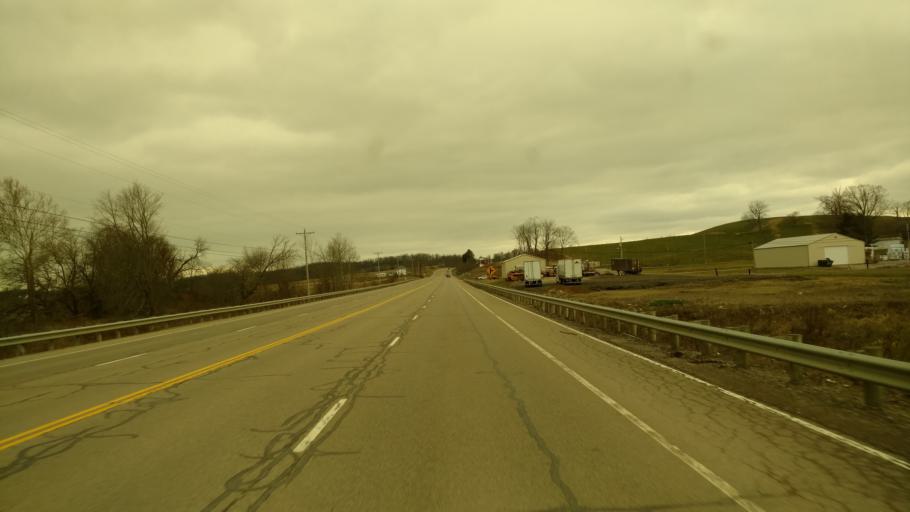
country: US
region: Ohio
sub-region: Perry County
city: Somerset
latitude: 39.9480
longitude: -82.2287
